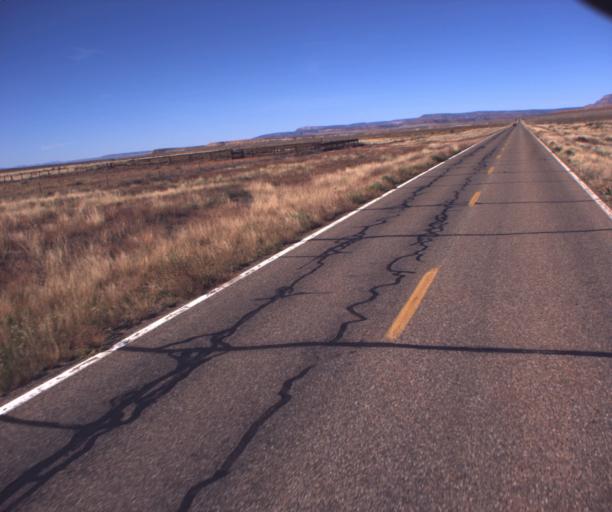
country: US
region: Arizona
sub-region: Coconino County
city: Fredonia
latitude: 36.9229
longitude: -112.4490
